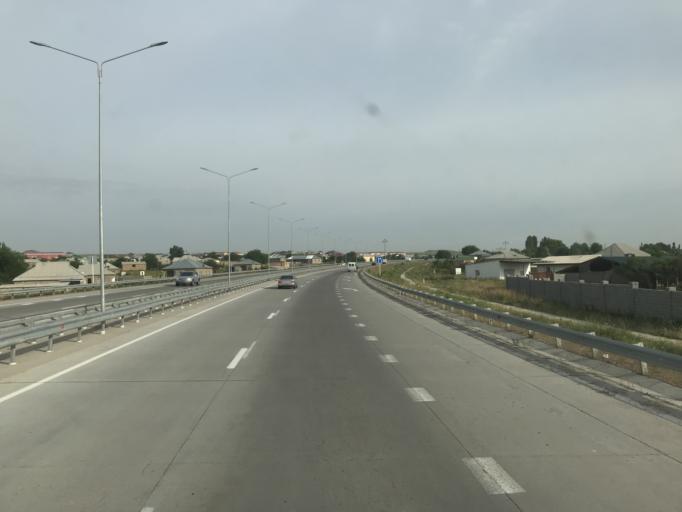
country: KZ
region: Ongtustik Qazaqstan
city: Qazyqurt
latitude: 41.7855
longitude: 69.3962
